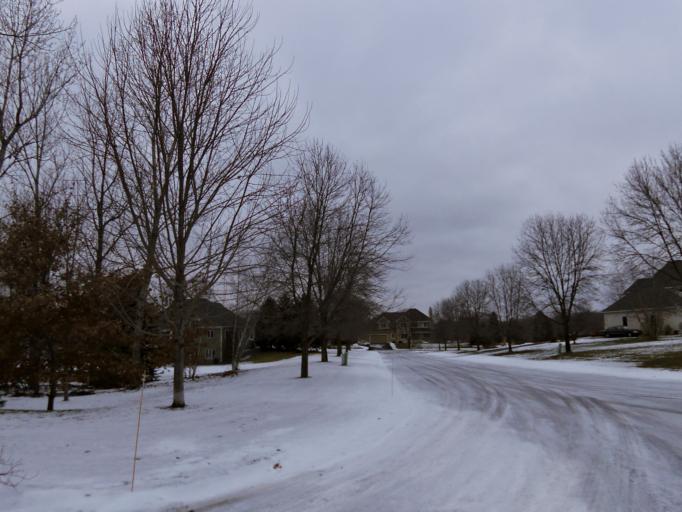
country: US
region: Minnesota
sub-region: Washington County
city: Lake Elmo
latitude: 44.9613
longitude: -92.8595
